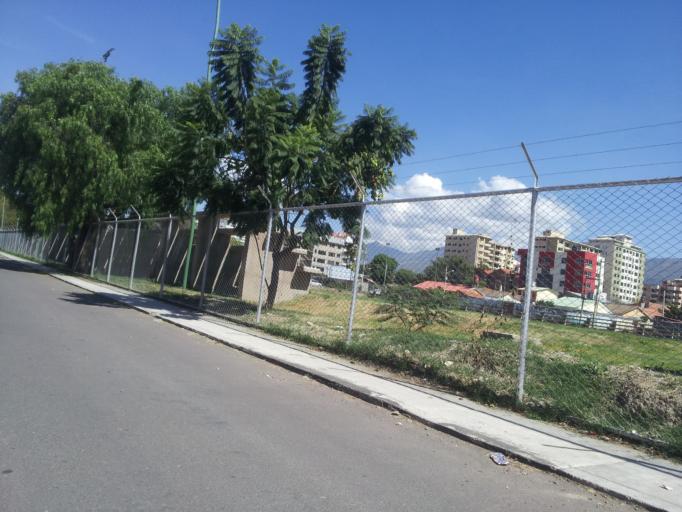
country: BO
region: Cochabamba
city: Cochabamba
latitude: -17.3745
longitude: -66.1747
